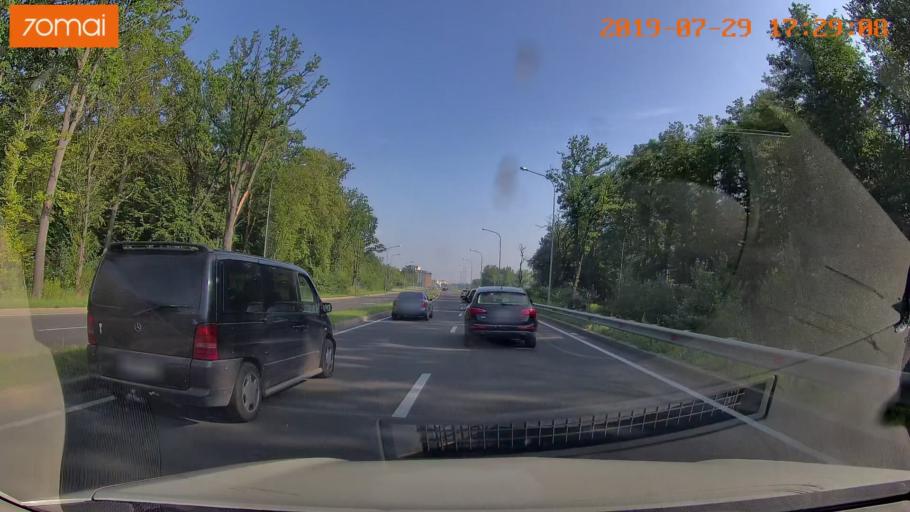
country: RU
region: Kaliningrad
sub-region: Gorod Kaliningrad
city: Kaliningrad
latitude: 54.7573
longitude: 20.4715
